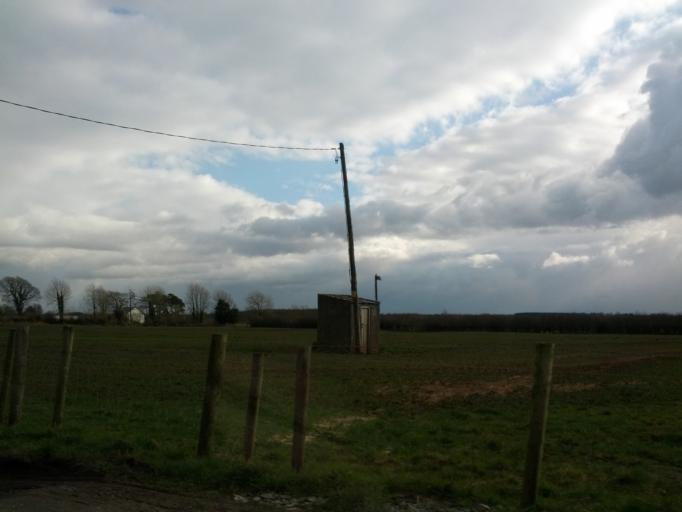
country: IE
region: Connaught
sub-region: County Galway
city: Athenry
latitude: 53.4311
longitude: -8.6503
